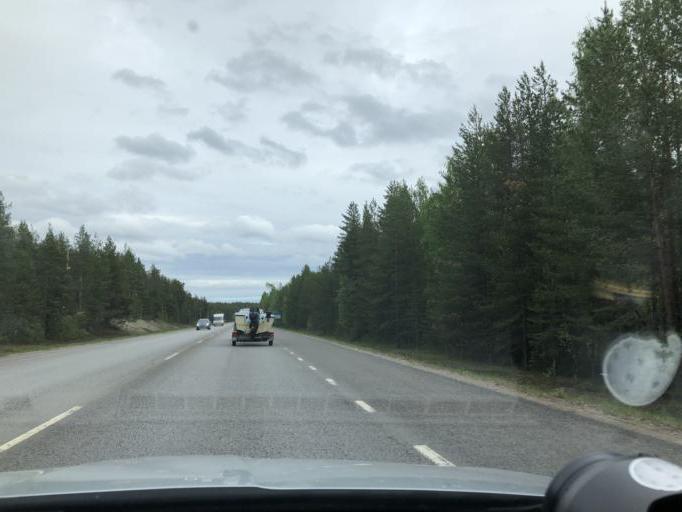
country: SE
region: Norrbotten
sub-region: Pitea Kommun
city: Pitea
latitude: 65.2737
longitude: 21.5221
